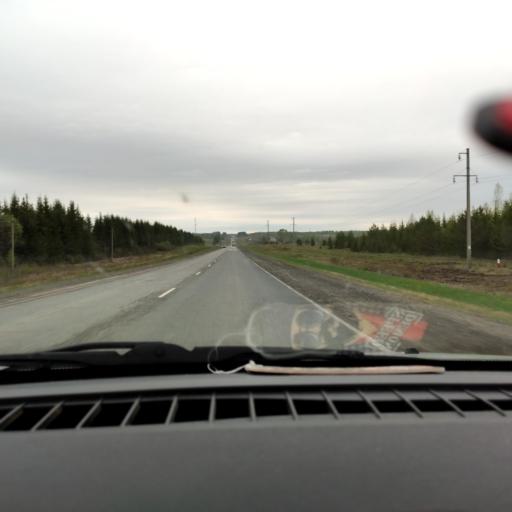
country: RU
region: Perm
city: Kudymkar
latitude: 58.8152
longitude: 54.6865
